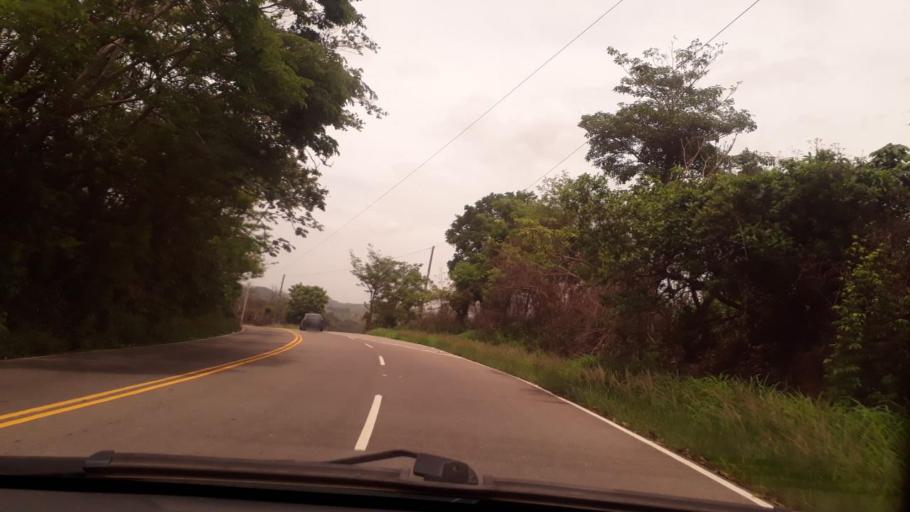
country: GT
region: Chiquimula
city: Quezaltepeque
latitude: 14.5878
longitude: -89.4551
